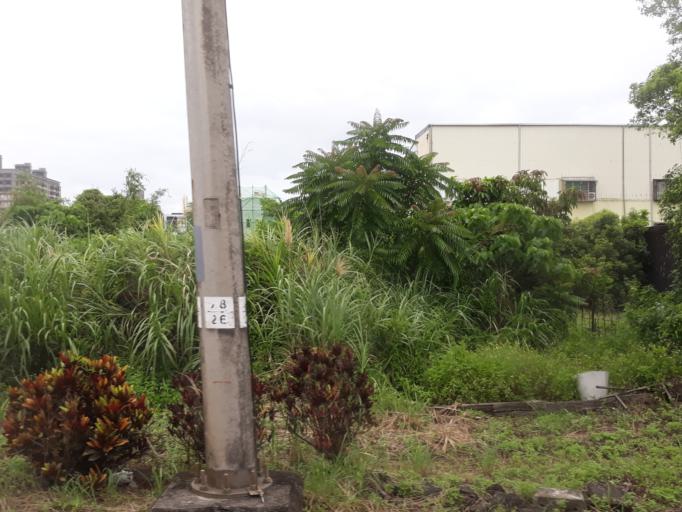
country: TW
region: Taiwan
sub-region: Yilan
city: Yilan
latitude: 24.6922
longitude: 121.7751
